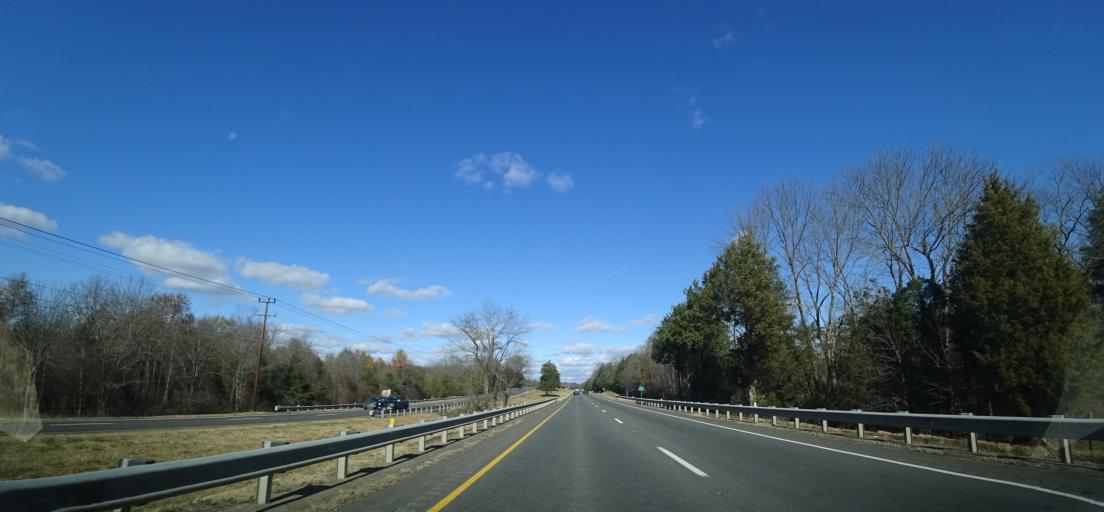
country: US
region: Virginia
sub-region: Fauquier County
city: Bealeton
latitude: 38.5669
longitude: -77.8013
